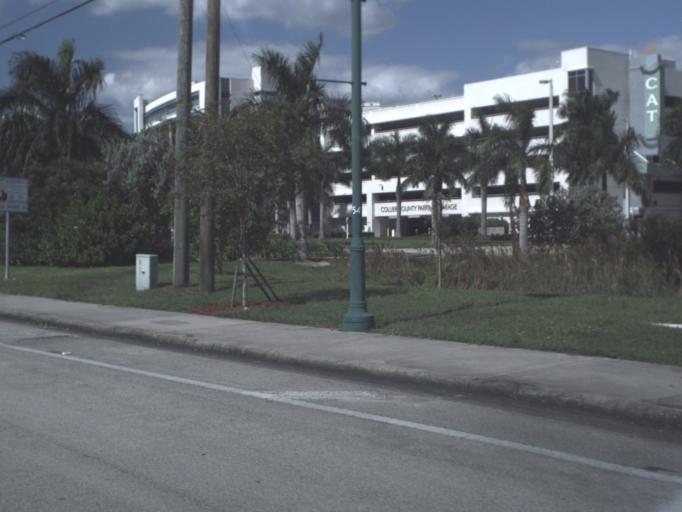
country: US
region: Florida
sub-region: Collier County
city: Naples
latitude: 26.1253
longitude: -81.7643
